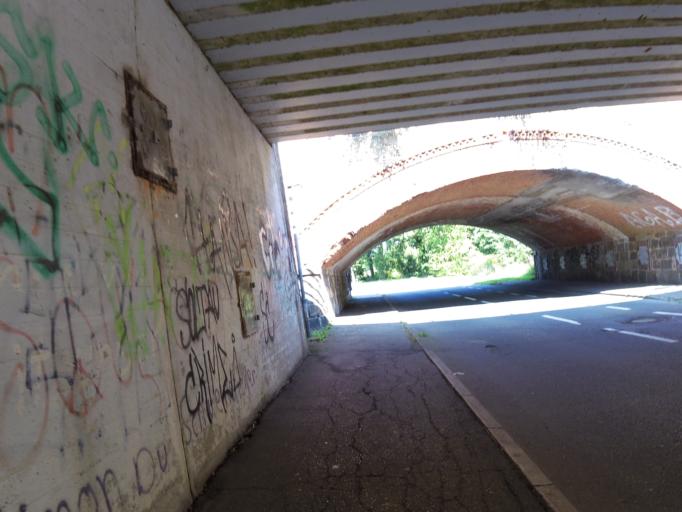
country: DE
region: Lower Saxony
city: Soltau
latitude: 52.9813
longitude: 9.8406
